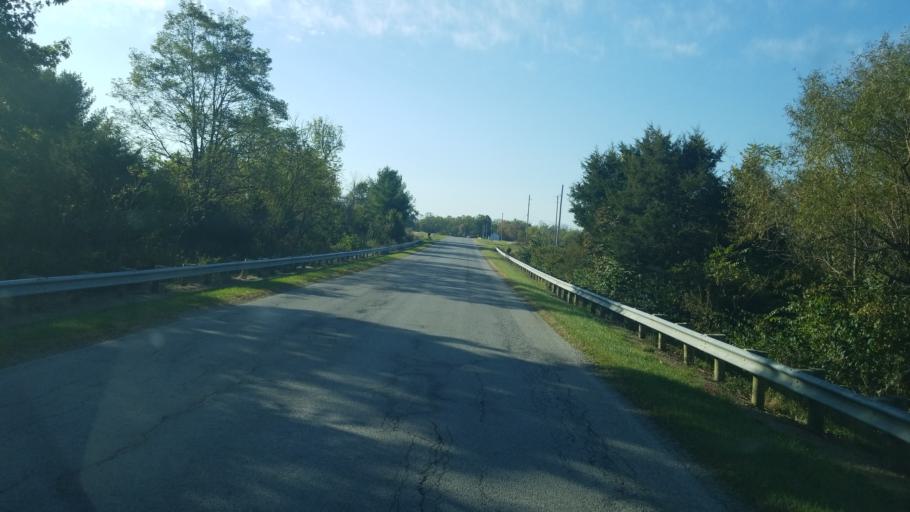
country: US
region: Ohio
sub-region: Morrow County
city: Cardington
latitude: 40.5213
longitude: -82.8640
